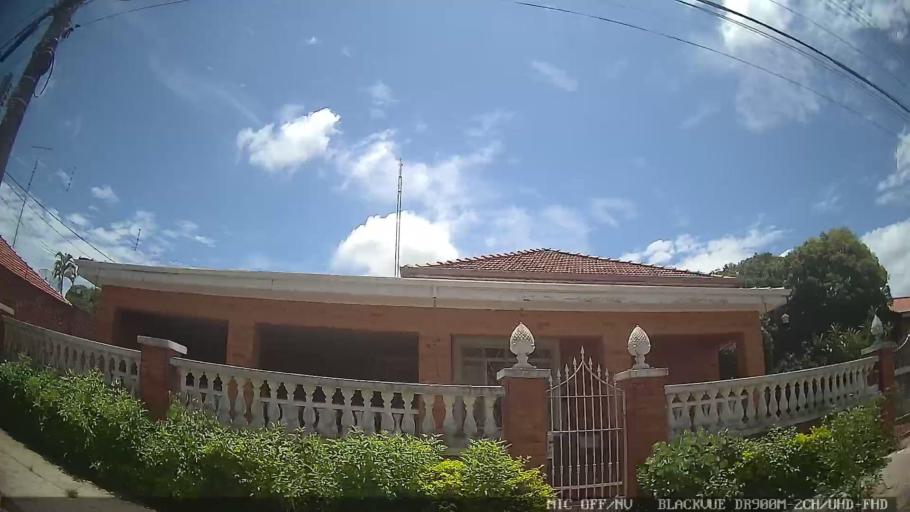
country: BR
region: Sao Paulo
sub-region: Laranjal Paulista
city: Laranjal Paulista
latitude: -23.0440
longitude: -47.8325
